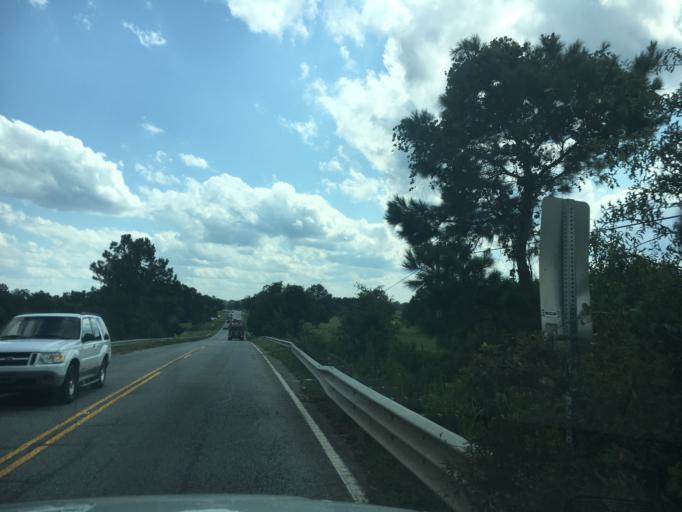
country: US
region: South Carolina
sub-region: Anderson County
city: Williamston
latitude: 34.5980
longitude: -82.4986
